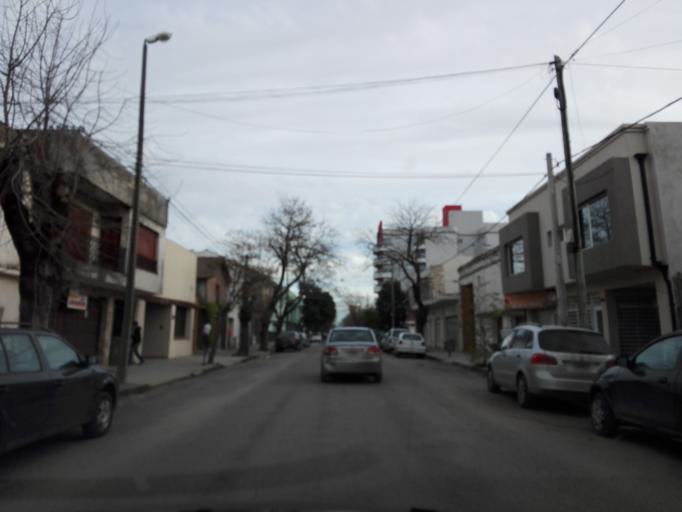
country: AR
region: Buenos Aires
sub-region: Partido de Balcarce
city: Balcarce
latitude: -37.8459
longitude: -58.2509
